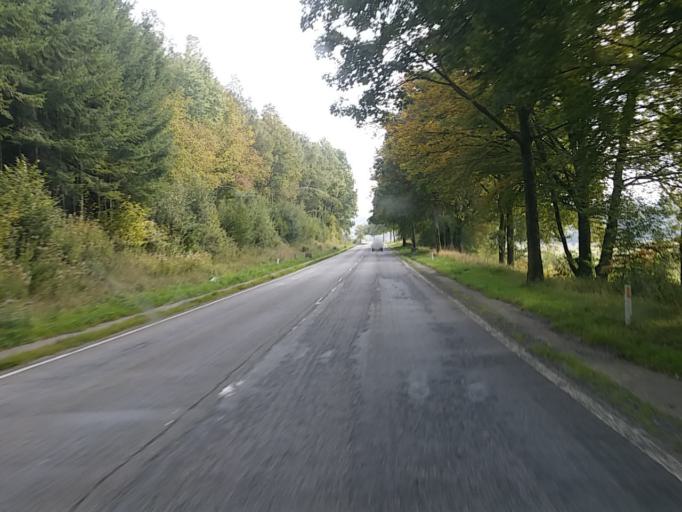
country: BE
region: Wallonia
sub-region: Province du Luxembourg
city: Chiny
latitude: 49.6887
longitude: 5.3951
